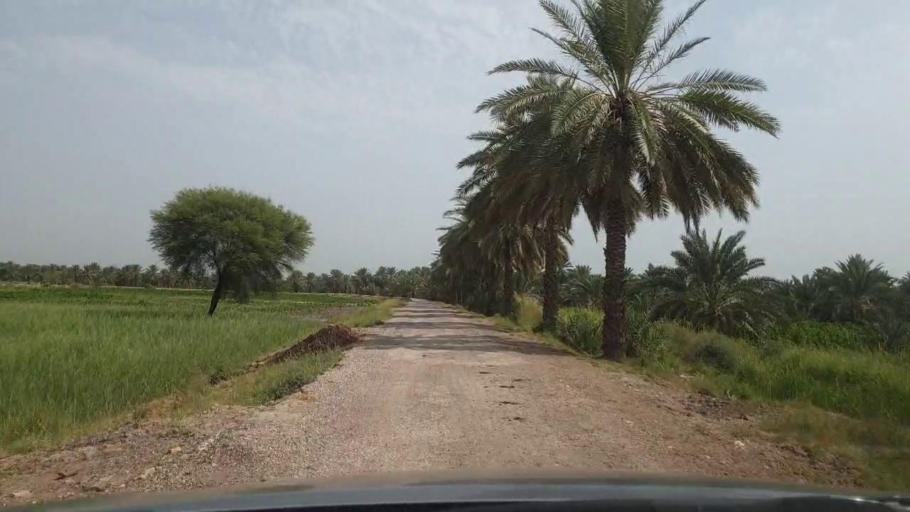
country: PK
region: Sindh
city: Rohri
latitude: 27.6832
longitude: 69.0360
